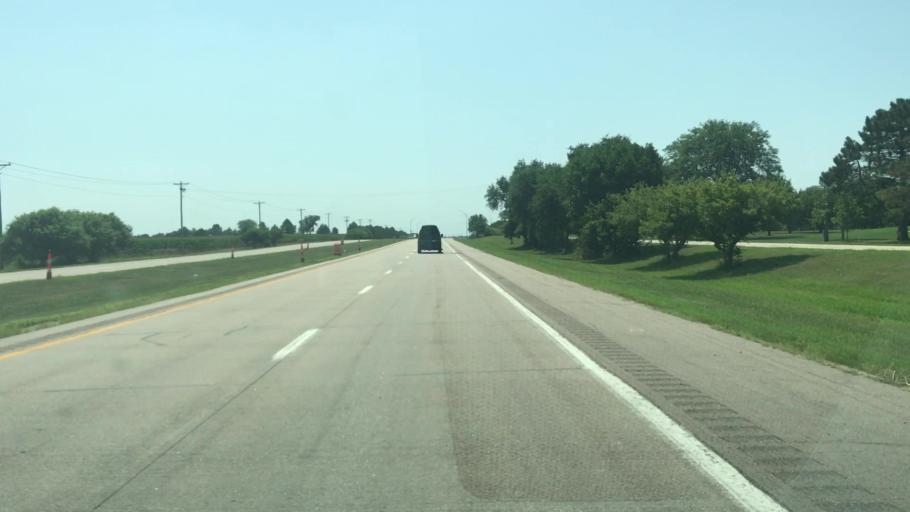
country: US
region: Nebraska
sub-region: Adams County
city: Hastings
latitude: 40.6376
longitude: -98.3820
